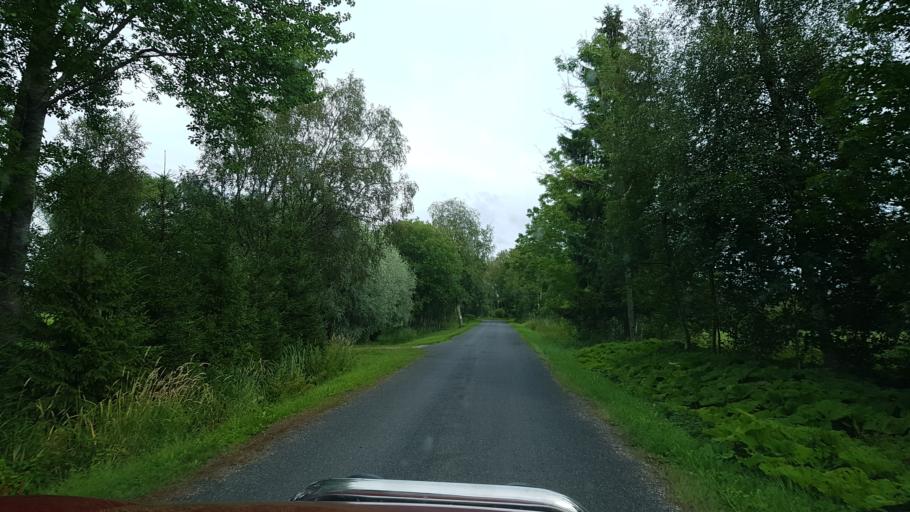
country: EE
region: Laeaene
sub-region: Ridala Parish
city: Uuemoisa
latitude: 58.9819
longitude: 23.8231
